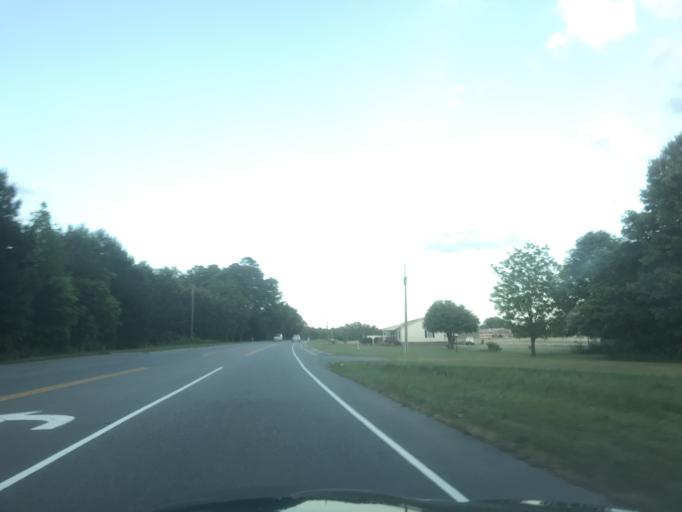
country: US
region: North Carolina
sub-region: Wake County
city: Wendell
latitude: 35.7695
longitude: -78.4151
